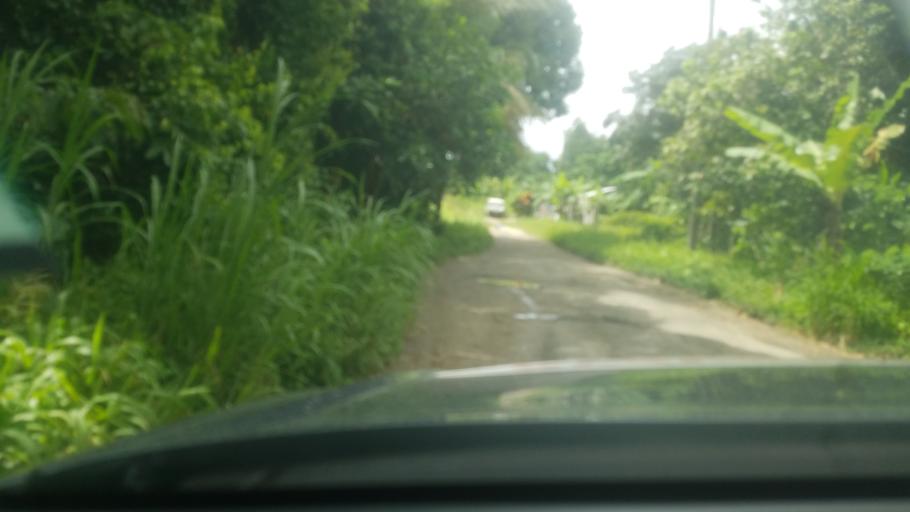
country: LC
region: Laborie Quarter
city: Laborie
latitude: 13.7779
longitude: -60.9790
